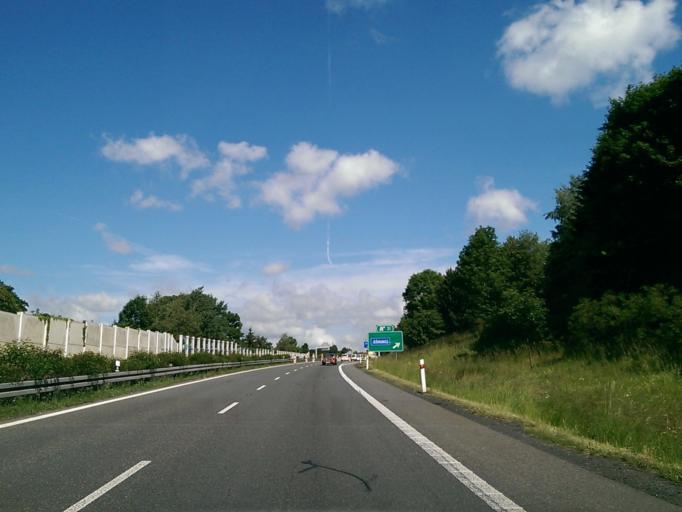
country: CZ
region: Liberecky
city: Hodkovice nad Mohelkou
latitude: 50.6978
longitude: 15.0994
